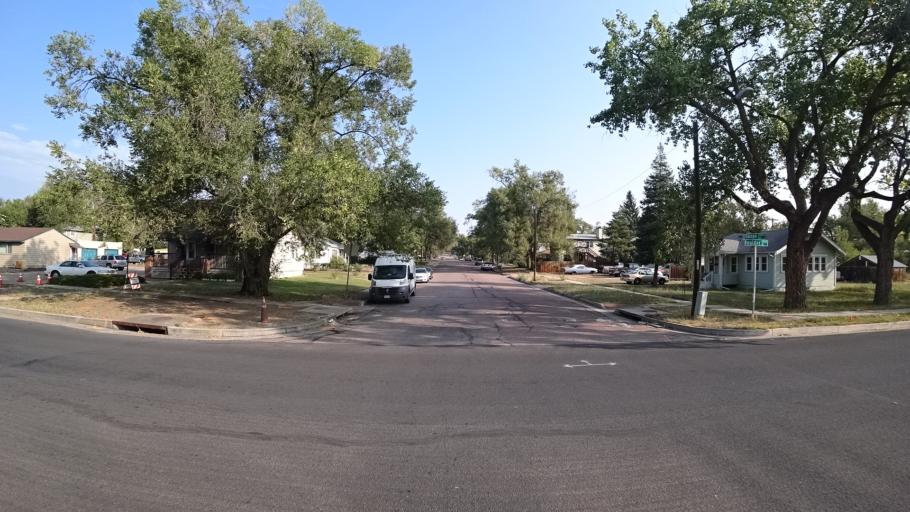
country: US
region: Colorado
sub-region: El Paso County
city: Colorado Springs
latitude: 38.8386
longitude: -104.7916
